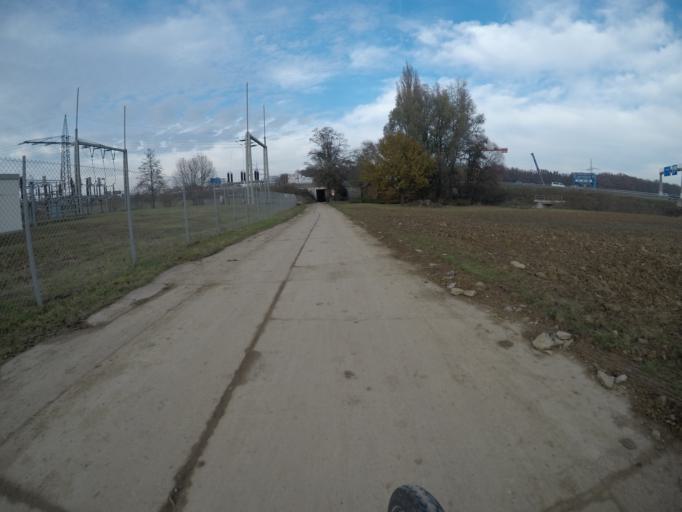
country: DE
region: Baden-Wuerttemberg
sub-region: Regierungsbezirk Stuttgart
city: Leinfelden-Echterdingen
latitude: 48.7033
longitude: 9.1729
